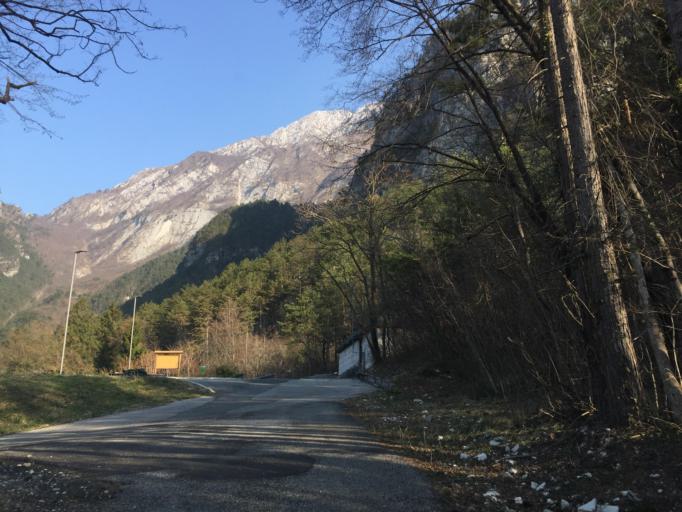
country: IT
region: Friuli Venezia Giulia
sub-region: Provincia di Udine
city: Amaro
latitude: 46.3778
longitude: 13.0922
